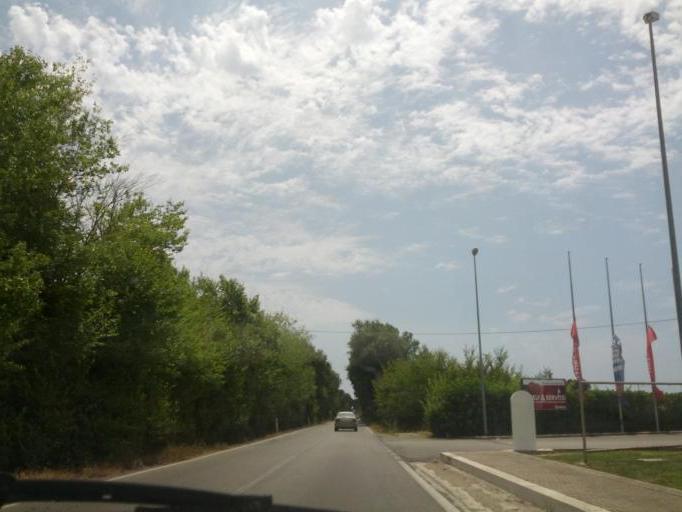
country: IT
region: Latium
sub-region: Provincia di Latina
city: Fondi
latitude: 41.3087
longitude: 13.3999
